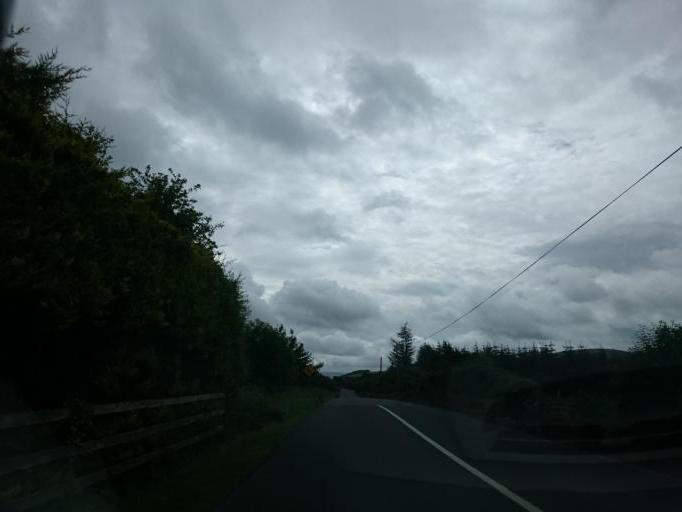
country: IE
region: Leinster
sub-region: Wicklow
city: Carnew
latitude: 52.8267
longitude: -6.5211
